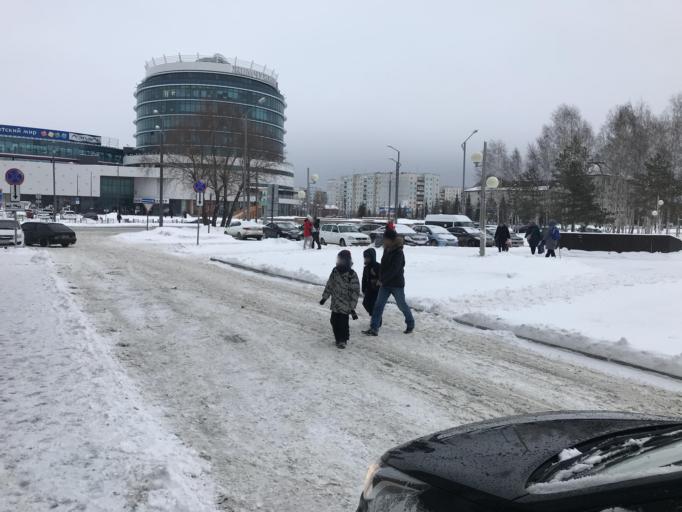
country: RU
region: Tjumen
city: Tobol'sk
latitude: 58.2272
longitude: 68.2747
